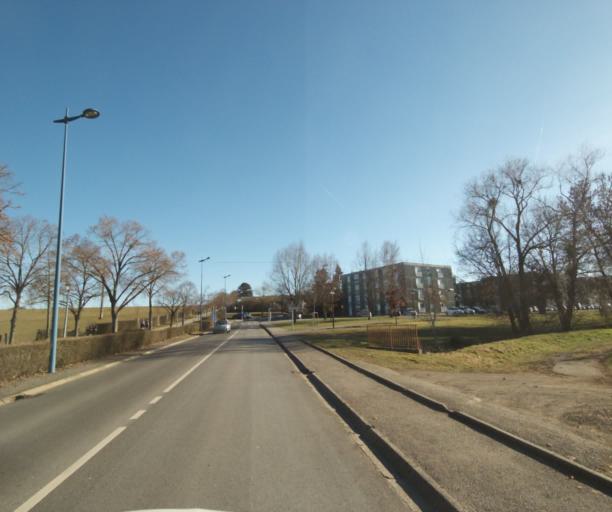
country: FR
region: Lorraine
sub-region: Departement de Meurthe-et-Moselle
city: Vandoeuvre-les-Nancy
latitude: 48.6472
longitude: 6.1968
